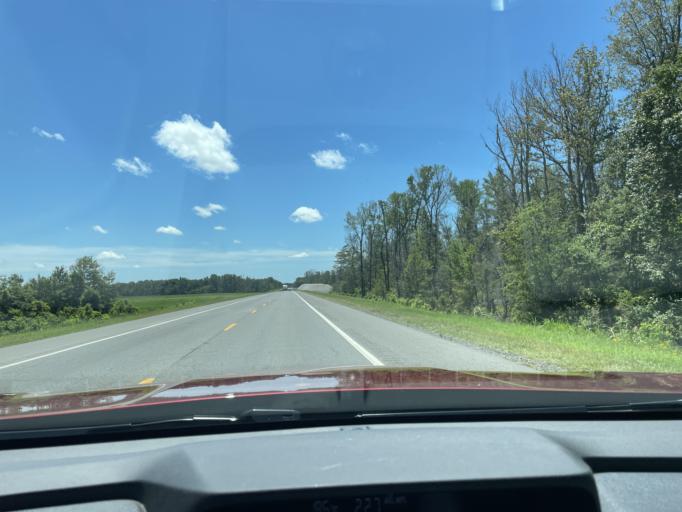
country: US
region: Arkansas
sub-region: Jefferson County
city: Pine Bluff
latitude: 34.1506
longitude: -91.9789
